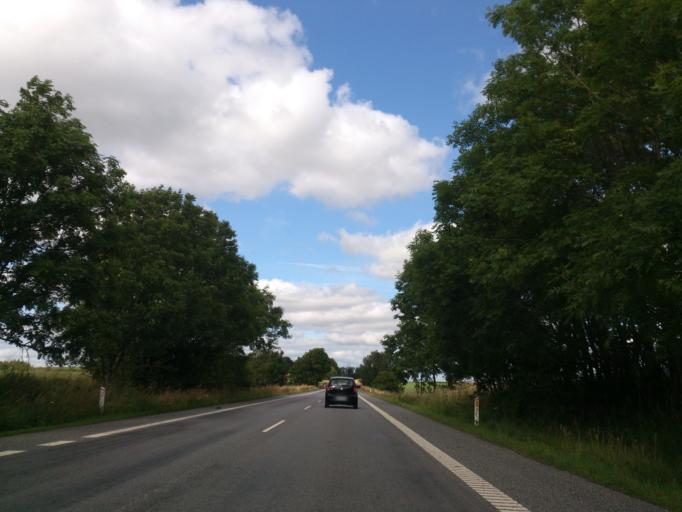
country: DK
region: South Denmark
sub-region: Aabenraa Kommune
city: Krusa
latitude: 54.9036
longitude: 9.4368
